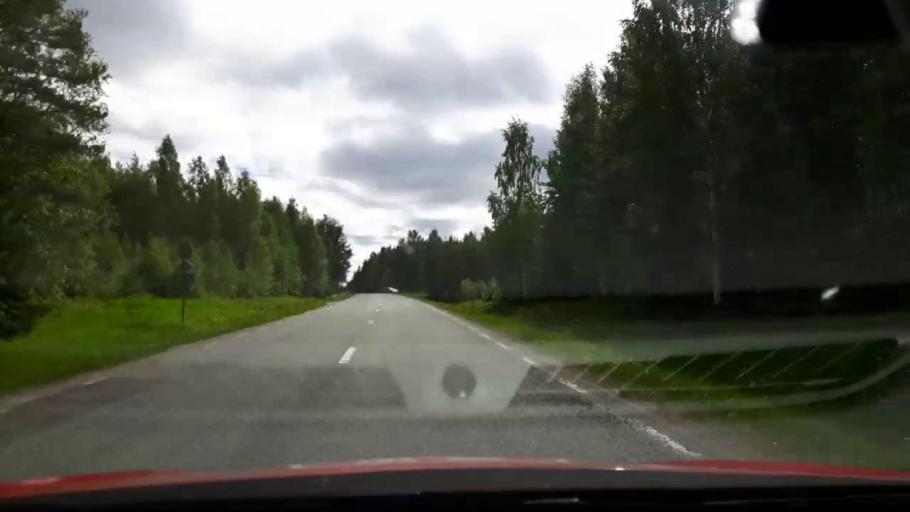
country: SE
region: Jaemtland
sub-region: Ragunda Kommun
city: Hammarstrand
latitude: 62.9912
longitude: 16.0954
